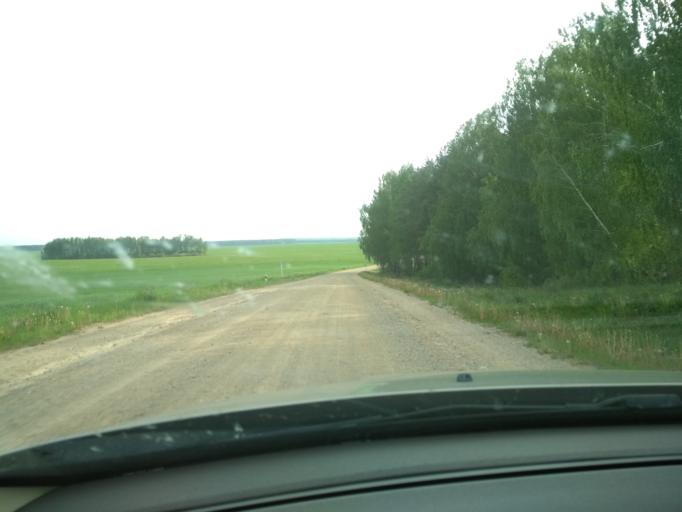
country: BY
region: Grodnenskaya
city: Mir
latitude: 53.3941
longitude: 26.4078
